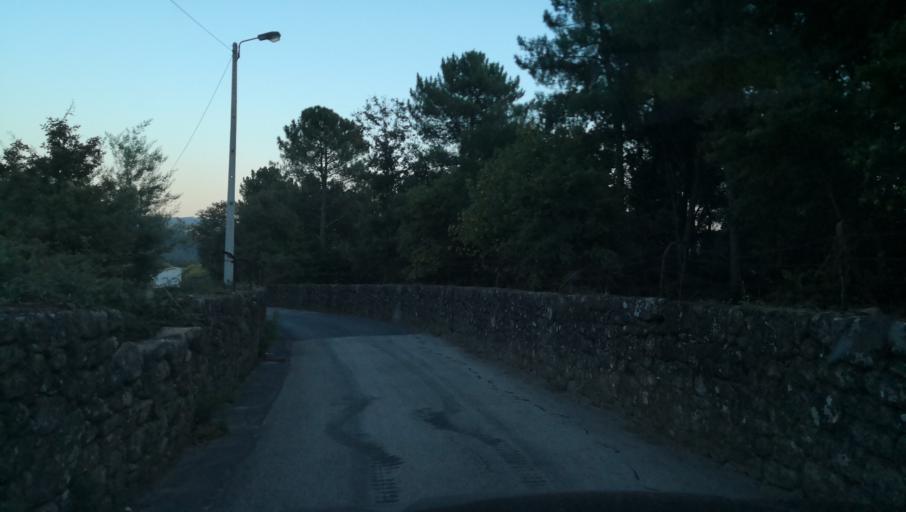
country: PT
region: Vila Real
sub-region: Vila Real
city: Vila Real
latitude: 41.3128
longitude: -7.7679
